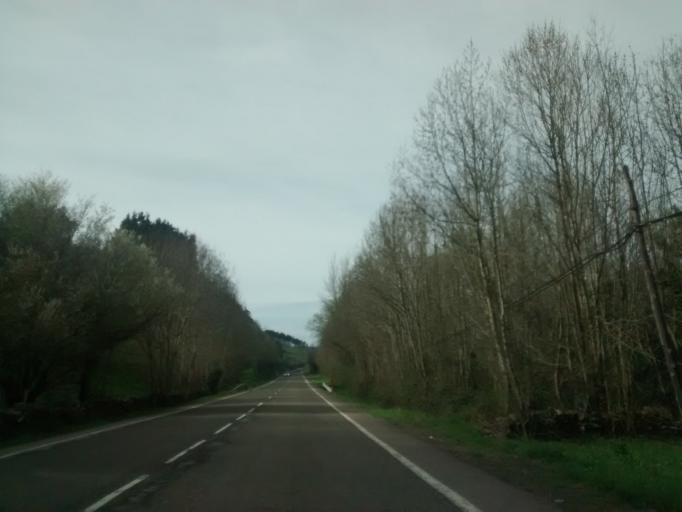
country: ES
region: Cantabria
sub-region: Provincia de Cantabria
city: Santiurde de Toranzo
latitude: 43.1747
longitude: -3.9025
